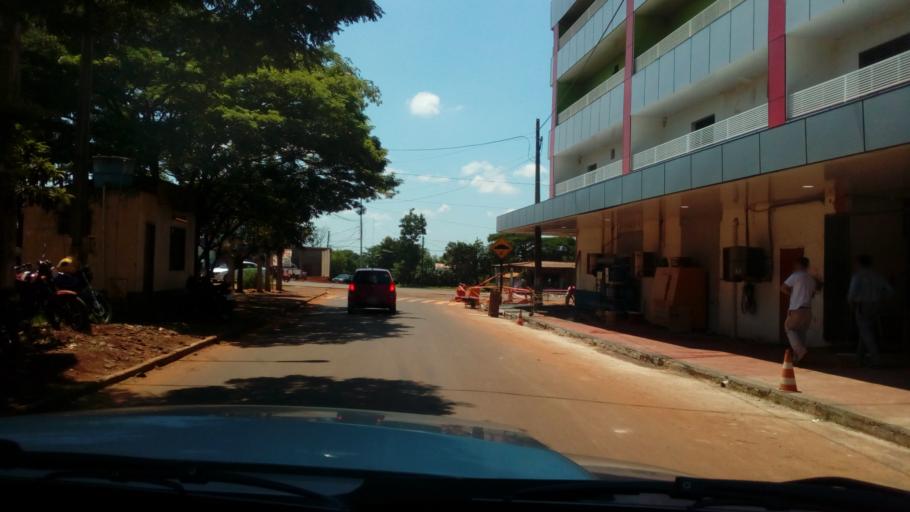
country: PY
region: Alto Parana
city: Ciudad del Este
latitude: -25.4857
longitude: -54.6623
